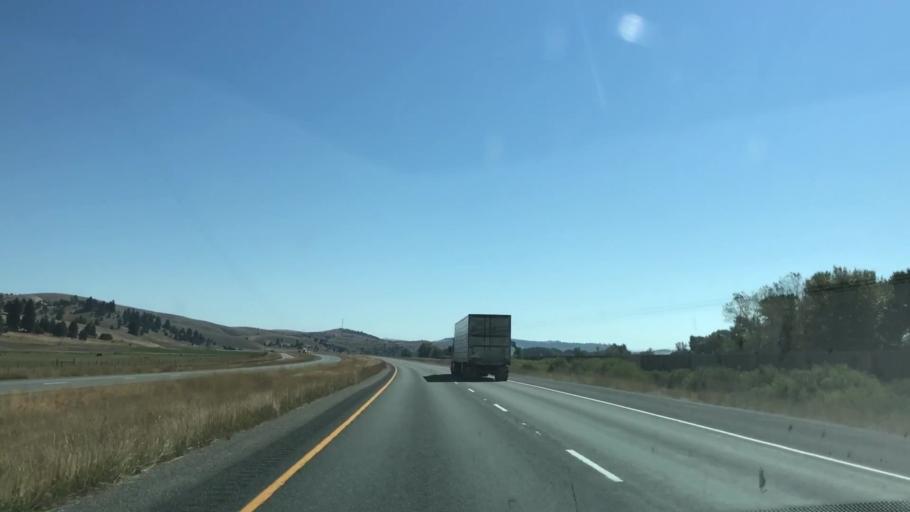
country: US
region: Montana
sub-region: Powell County
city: Deer Lodge
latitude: 46.6020
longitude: -112.9617
